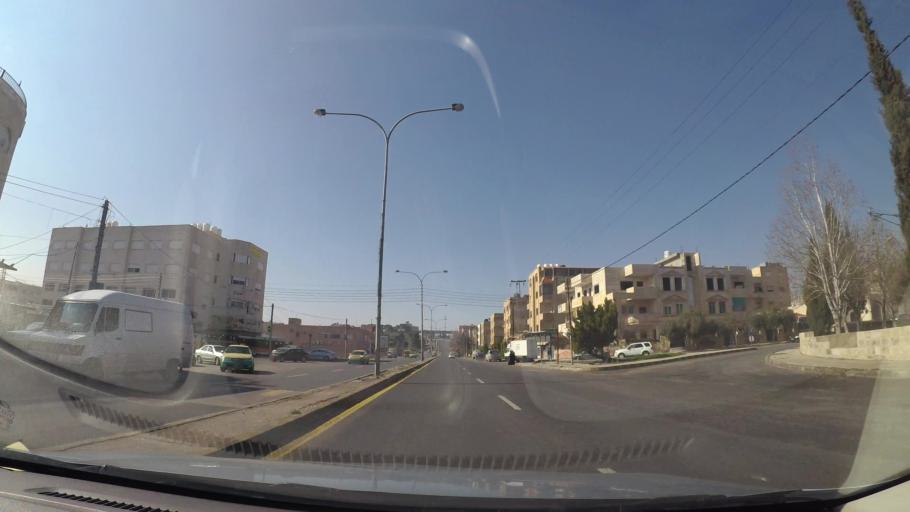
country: JO
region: Amman
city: Al Bunayyat ash Shamaliyah
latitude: 31.9238
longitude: 35.8977
